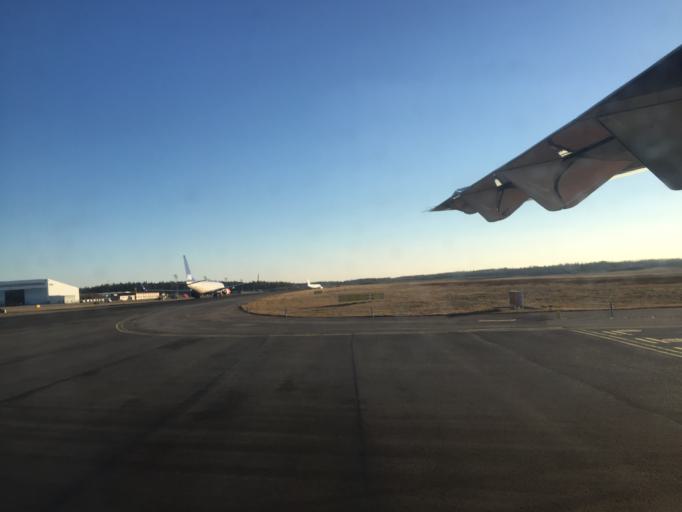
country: SE
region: Stockholm
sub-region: Sigtuna Kommun
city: Marsta
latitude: 59.6441
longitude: 17.9186
